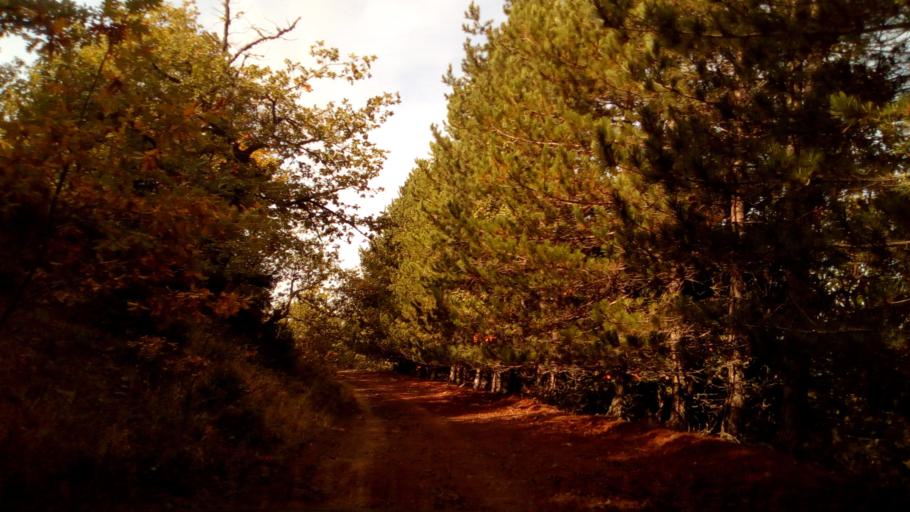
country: GR
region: Central Greece
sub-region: Nomos Fokidos
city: Lidoriki
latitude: 38.4736
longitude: 22.0433
